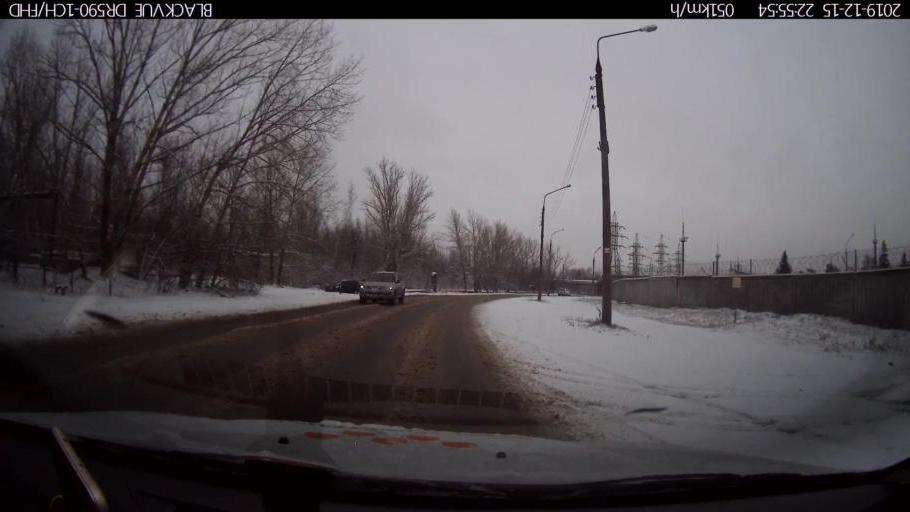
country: RU
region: Nizjnij Novgorod
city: Neklyudovo
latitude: 56.3540
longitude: 43.8952
